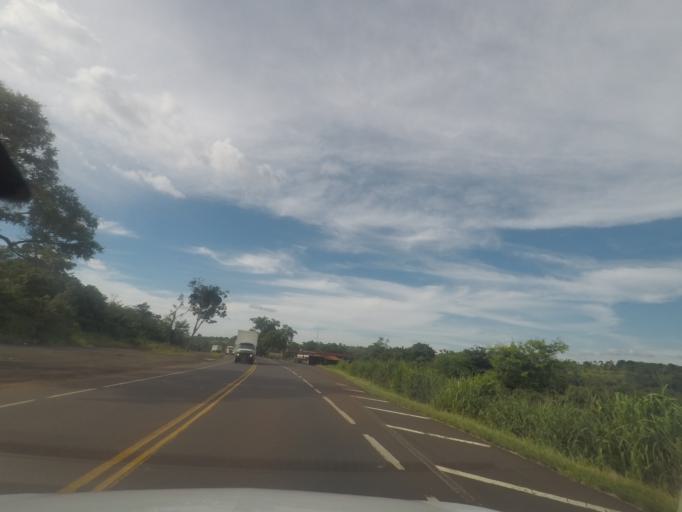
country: BR
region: Minas Gerais
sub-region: Monte Alegre De Minas
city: Monte Alegre de Minas
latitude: -19.0438
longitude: -49.0098
